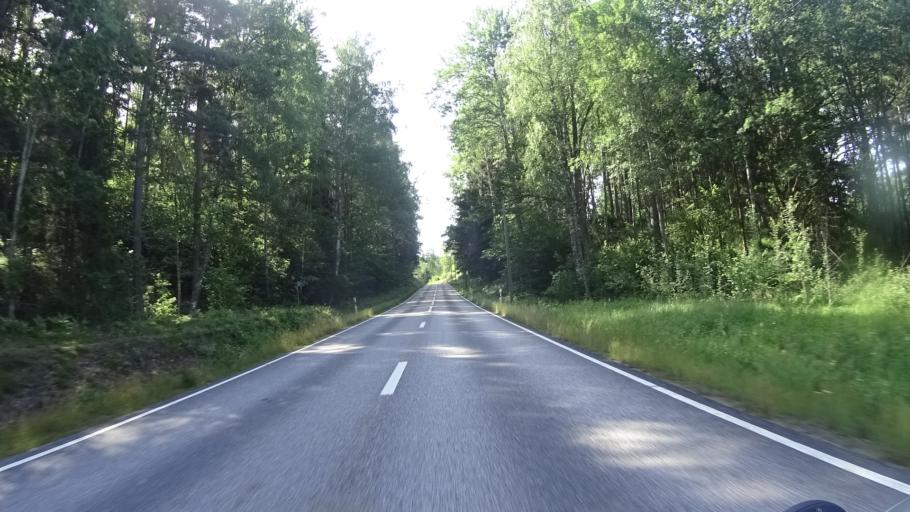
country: SE
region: Kalmar
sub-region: Vasterviks Kommun
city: Overum
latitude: 58.0350
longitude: 16.2301
